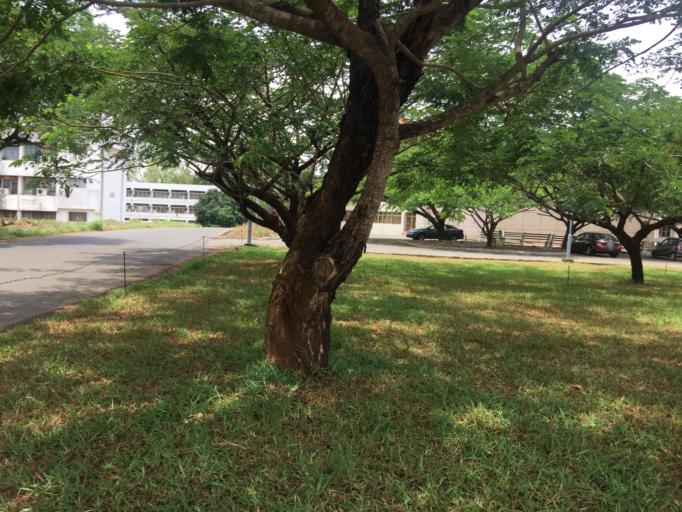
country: GH
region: Greater Accra
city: Medina Estates
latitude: 5.6533
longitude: -0.1834
